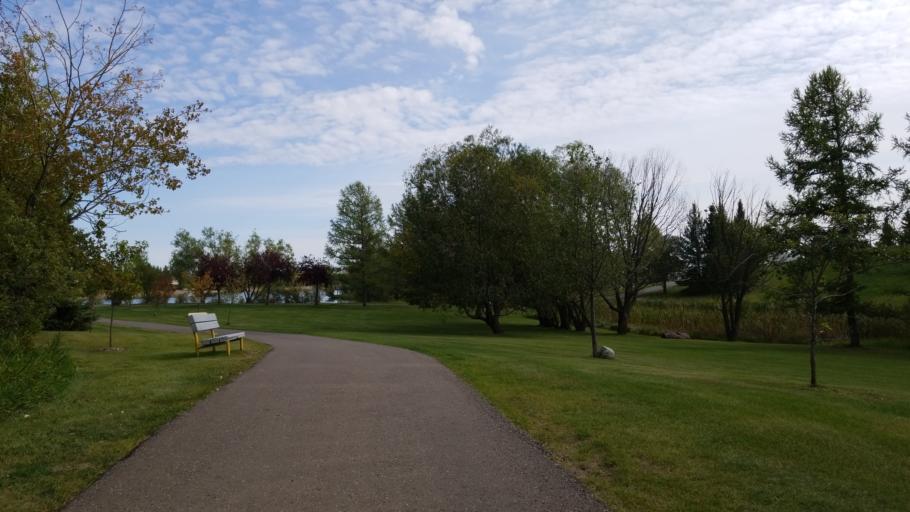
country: CA
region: Saskatchewan
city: Lloydminster
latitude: 53.2603
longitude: -110.0429
